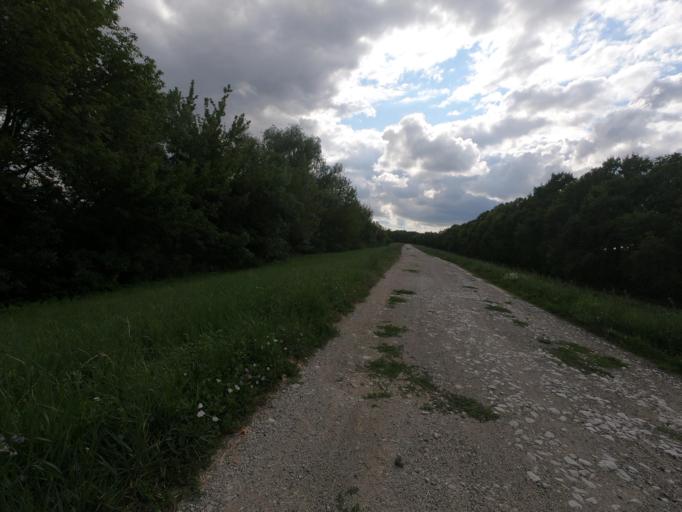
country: HU
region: Heves
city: Poroszlo
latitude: 47.6735
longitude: 20.7065
